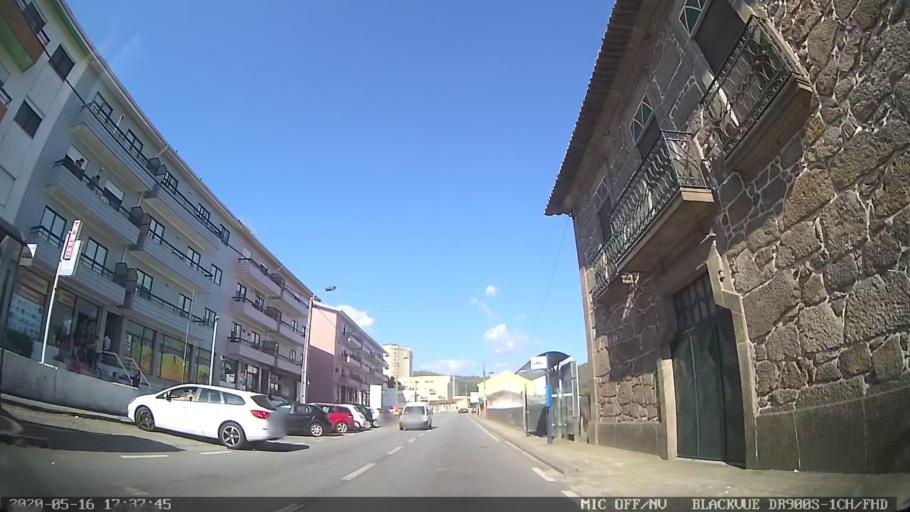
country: PT
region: Porto
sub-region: Gondomar
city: Fanzeres
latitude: 41.1827
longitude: -8.5288
